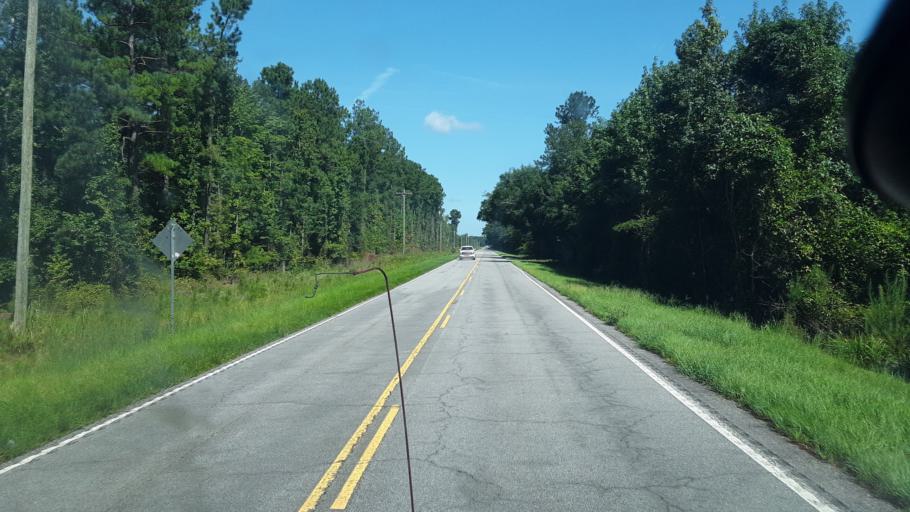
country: US
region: South Carolina
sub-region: Hampton County
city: Hampton
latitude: 32.9693
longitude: -81.0485
